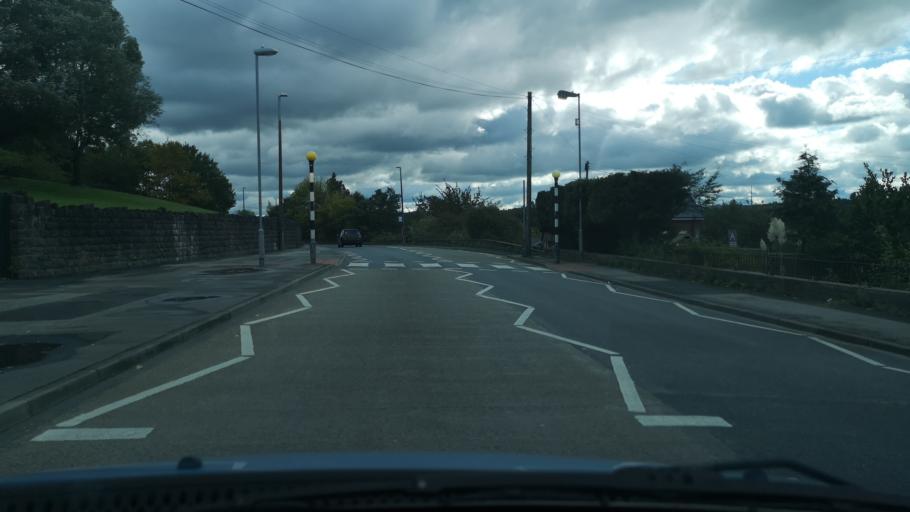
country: GB
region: England
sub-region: Kirklees
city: Batley
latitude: 53.6899
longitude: -1.6542
